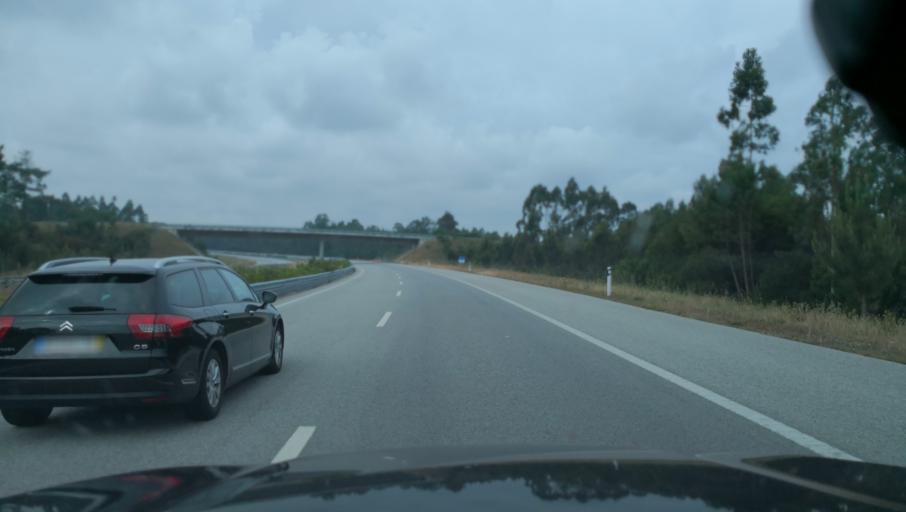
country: PT
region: Coimbra
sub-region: Figueira da Foz
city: Alhadas
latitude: 40.2479
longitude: -8.7804
